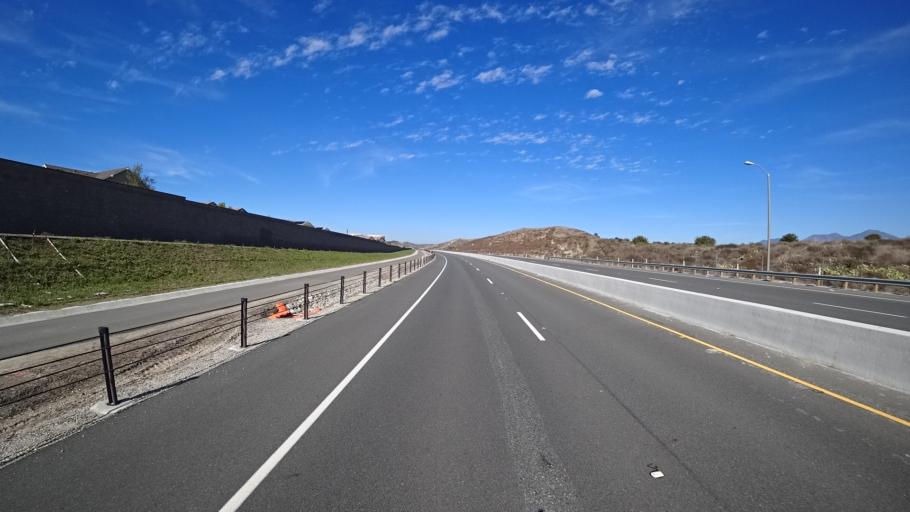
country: US
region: California
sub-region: Orange County
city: Ladera Ranch
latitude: 33.5534
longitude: -117.5962
